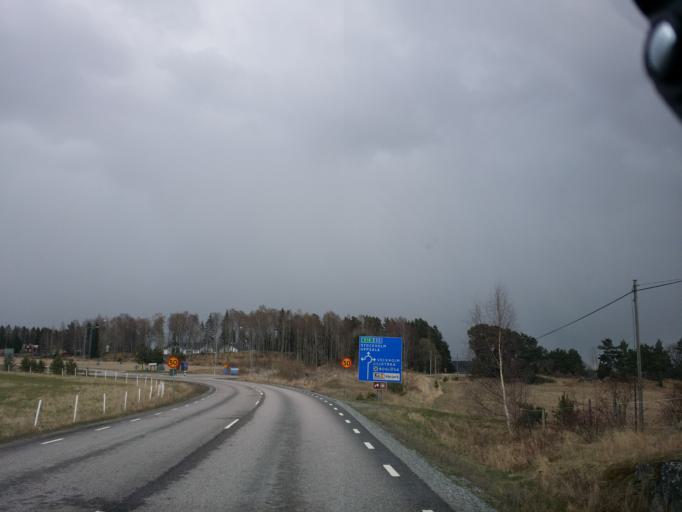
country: SE
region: Uppsala
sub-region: Enkopings Kommun
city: Enkoping
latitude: 59.6195
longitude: 17.1165
